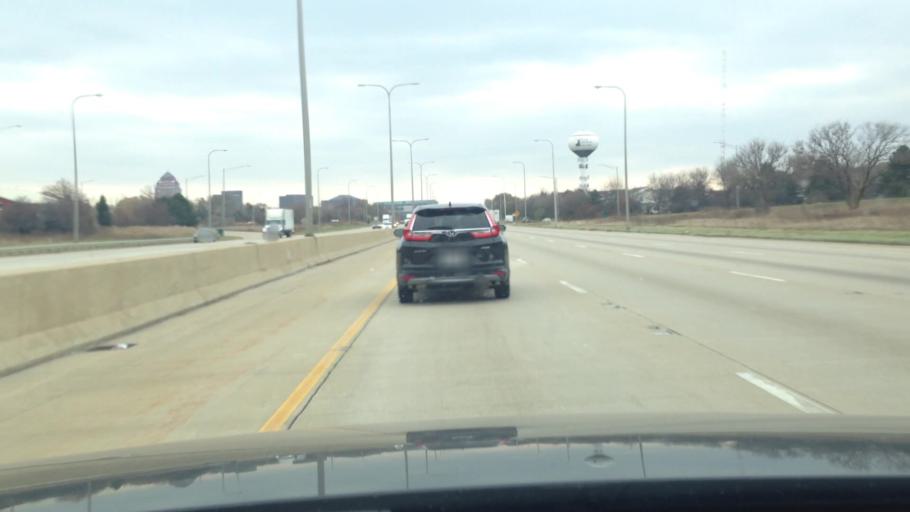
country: US
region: Illinois
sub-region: DuPage County
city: Itasca
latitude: 42.0031
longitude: -88.0267
